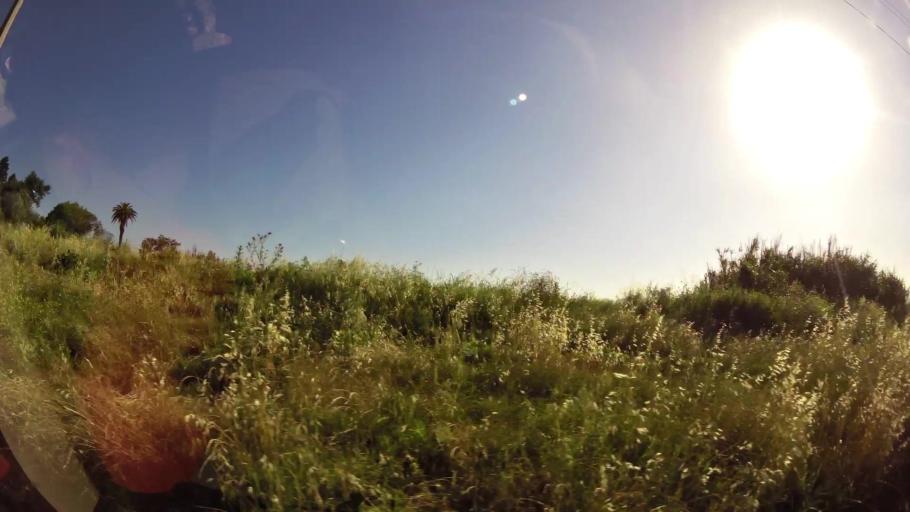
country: UY
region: Canelones
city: La Paz
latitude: -34.8175
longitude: -56.2172
